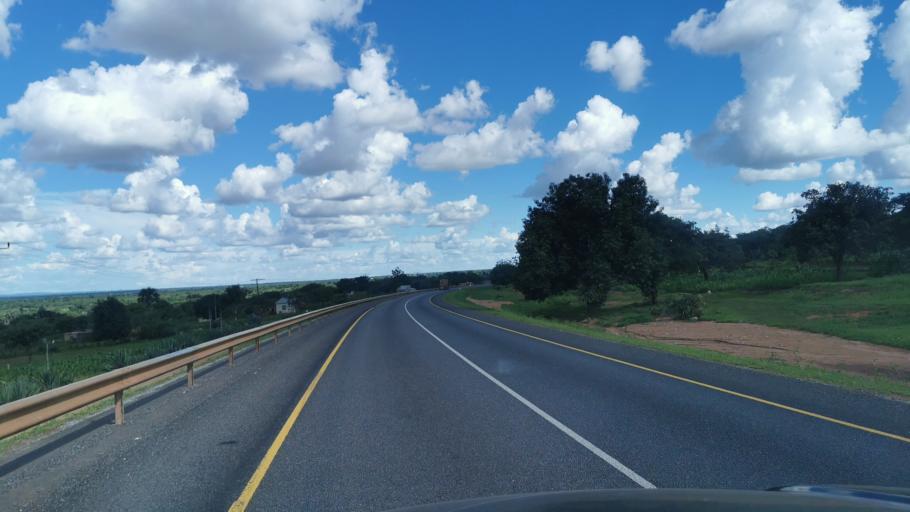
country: TZ
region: Geita
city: Ushirombo
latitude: -3.4351
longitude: 31.8310
